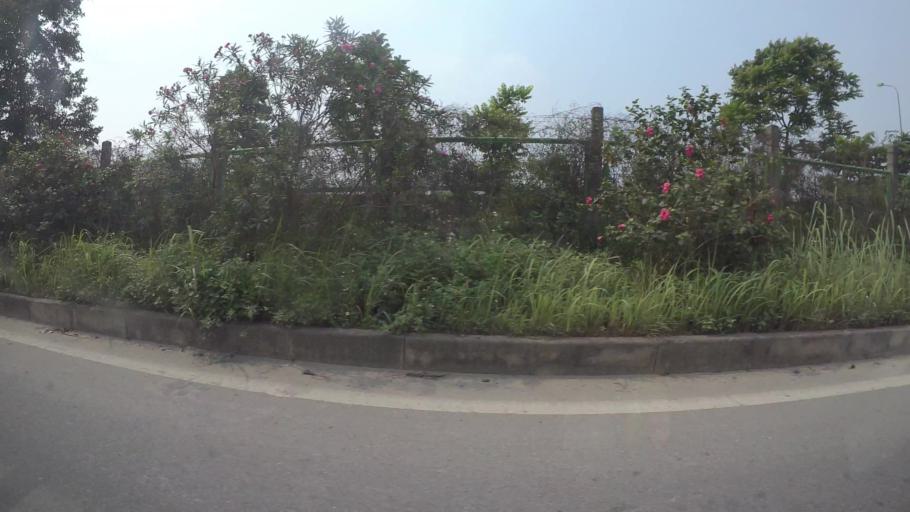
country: VN
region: Ha Noi
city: Quoc Oai
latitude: 21.0017
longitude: 105.6114
